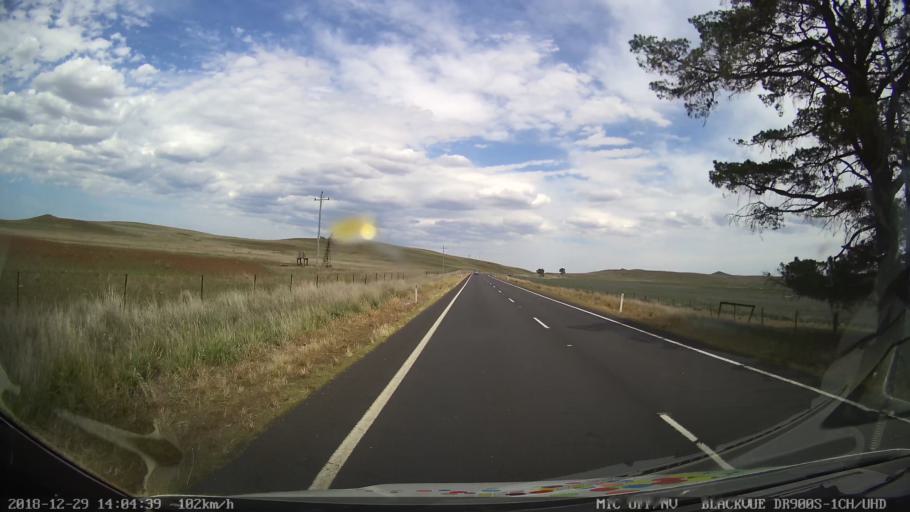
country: AU
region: New South Wales
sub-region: Cooma-Monaro
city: Cooma
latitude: -36.3195
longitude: 149.1879
